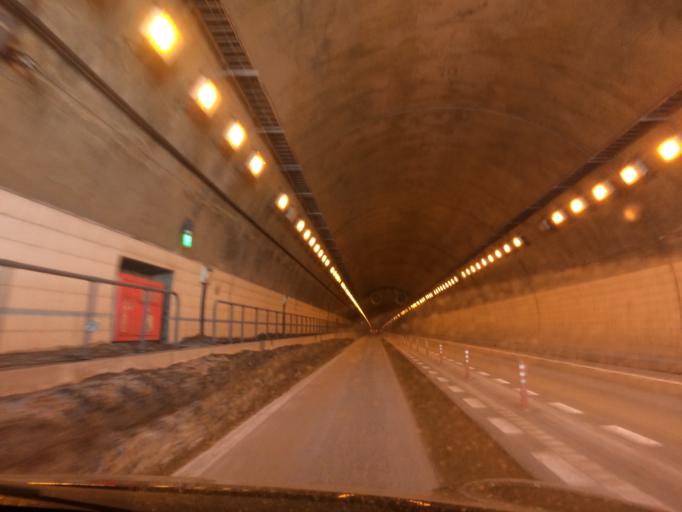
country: JP
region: Hokkaido
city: Shimo-furano
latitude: 43.0572
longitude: 142.7074
